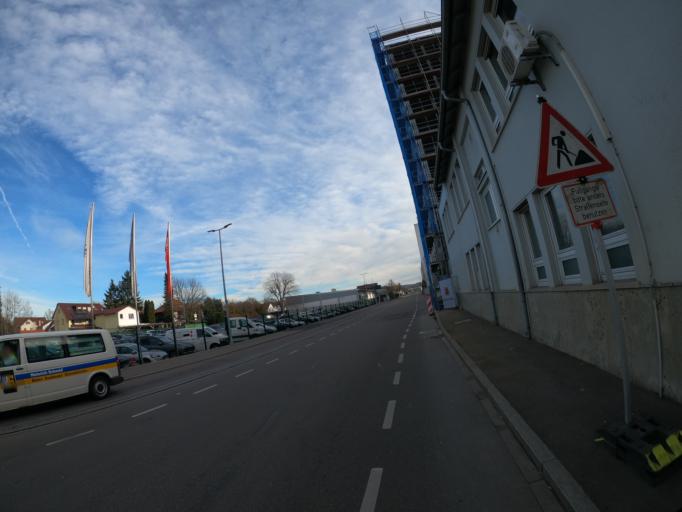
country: DE
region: Baden-Wuerttemberg
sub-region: Regierungsbezirk Stuttgart
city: Eislingen
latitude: 48.6967
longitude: 9.7092
